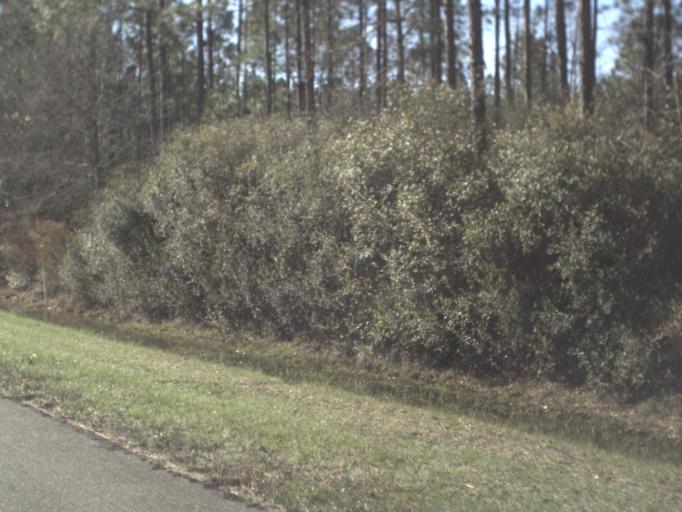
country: US
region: Florida
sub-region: Calhoun County
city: Blountstown
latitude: 30.4264
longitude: -85.1171
